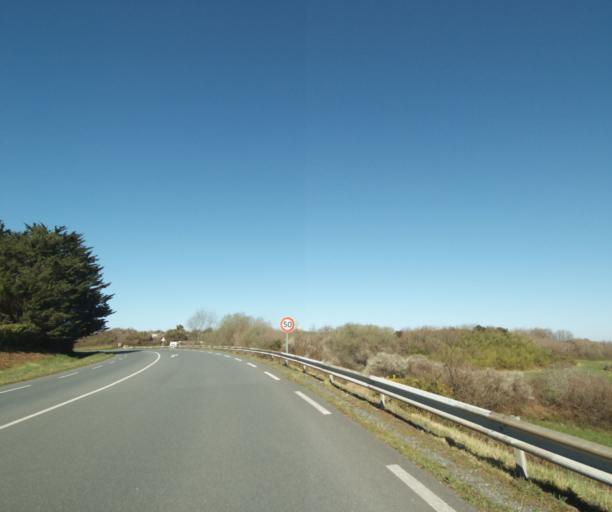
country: FR
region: Aquitaine
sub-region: Departement des Pyrenees-Atlantiques
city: Ciboure
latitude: 43.3889
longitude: -1.6998
